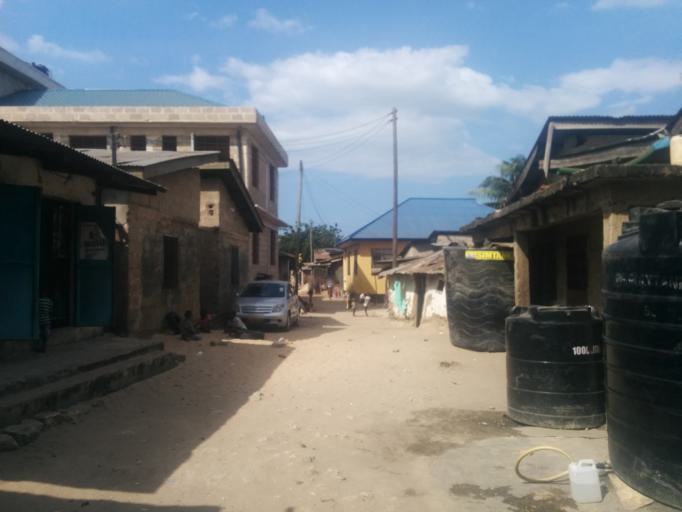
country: TZ
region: Dar es Salaam
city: Magomeni
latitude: -6.7967
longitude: 39.2363
